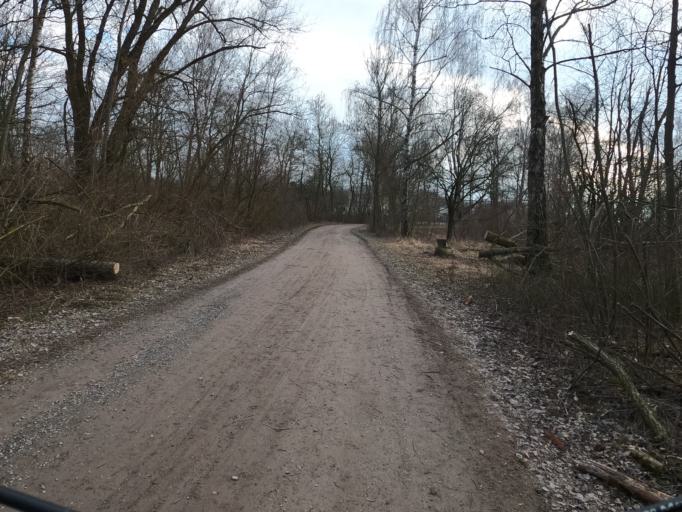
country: DE
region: Bavaria
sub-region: Swabia
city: Nersingen
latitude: 48.4412
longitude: 10.1094
